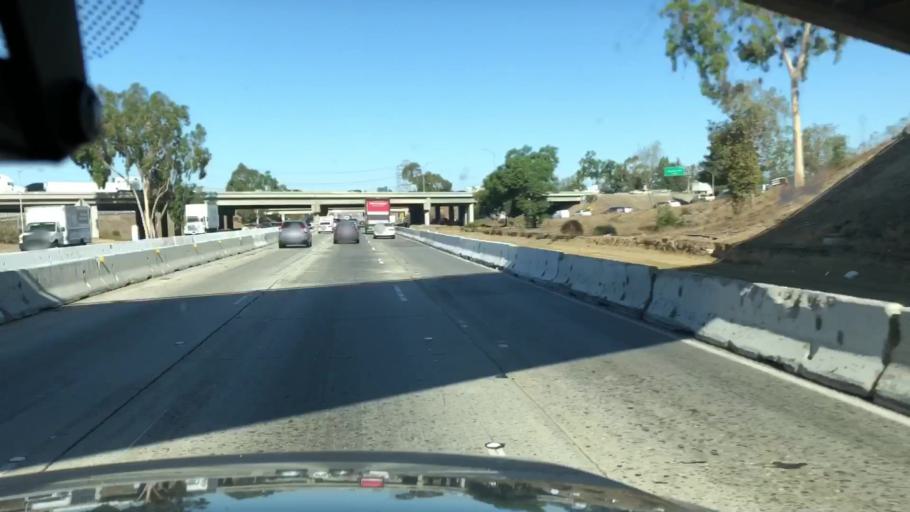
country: US
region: California
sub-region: Los Angeles County
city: Santa Fe Springs
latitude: 33.9397
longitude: -118.0955
